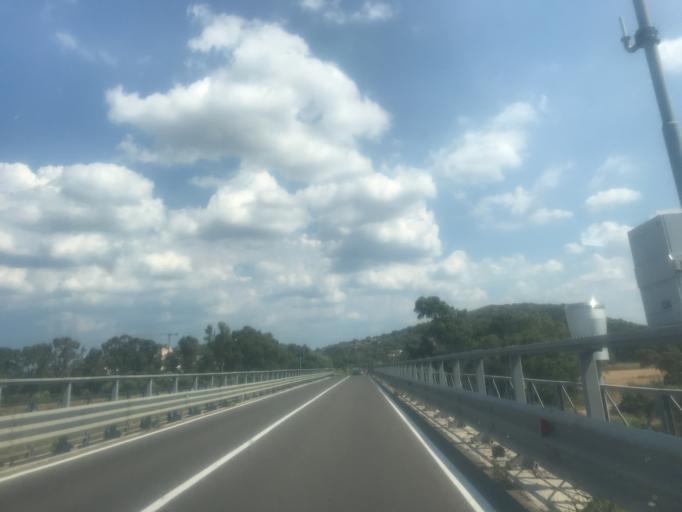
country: IT
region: Sardinia
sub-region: Provincia di Olbia-Tempio
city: Olbia
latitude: 40.9040
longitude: 9.5376
